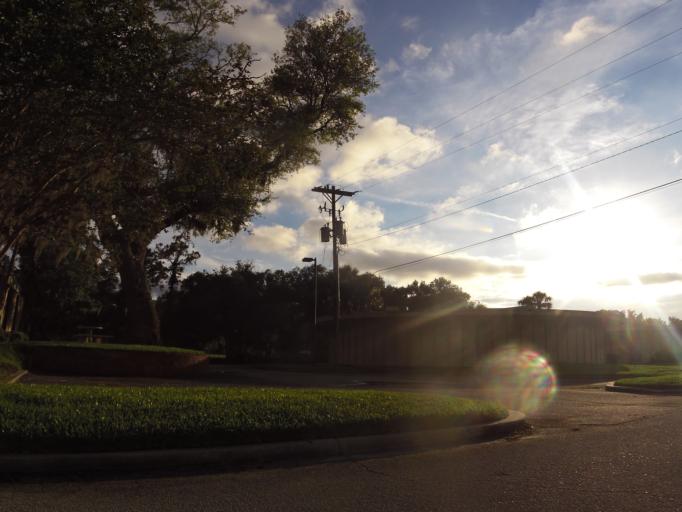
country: US
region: Florida
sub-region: Duval County
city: Jacksonville
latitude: 30.3012
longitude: -81.6209
